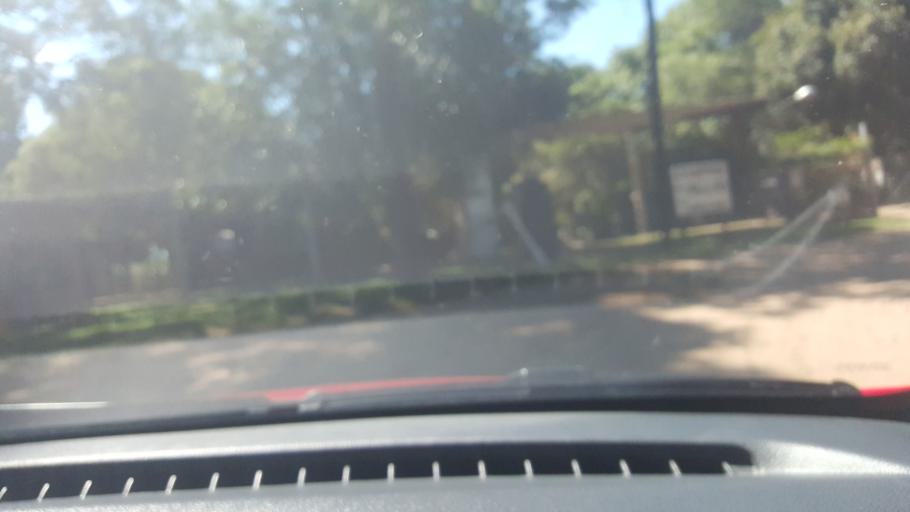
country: AR
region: Corrientes
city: Ituzaingo
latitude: -27.5943
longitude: -56.7103
